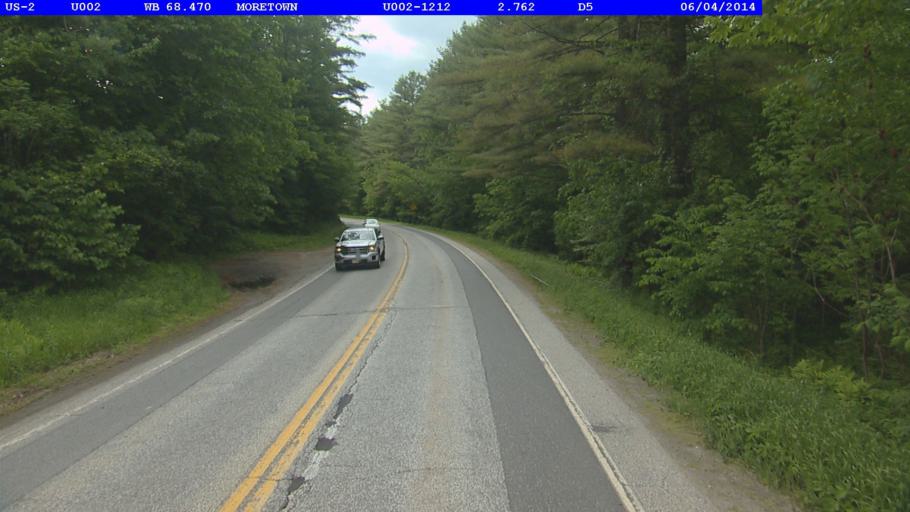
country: US
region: Vermont
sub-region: Washington County
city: Waterbury
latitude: 44.3121
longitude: -72.7003
